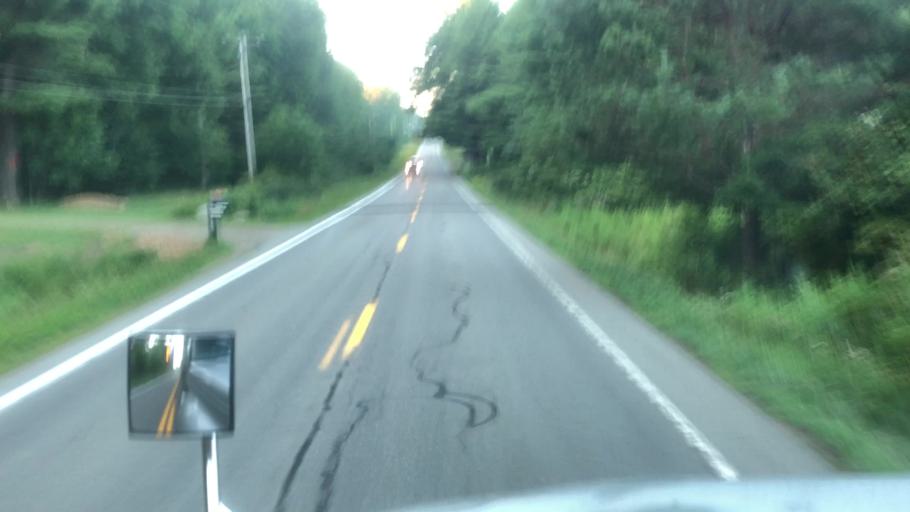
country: US
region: Pennsylvania
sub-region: Crawford County
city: Titusville
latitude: 41.5875
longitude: -79.6098
